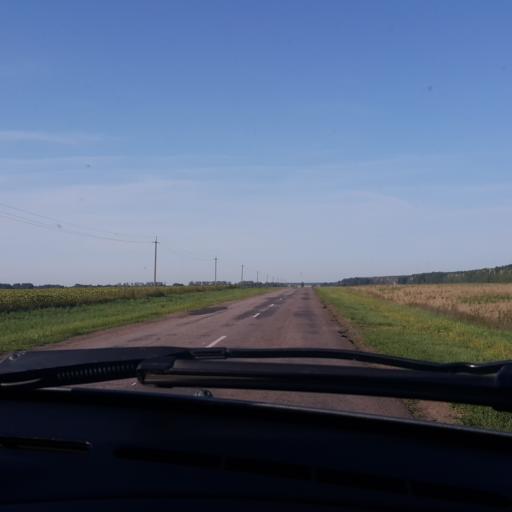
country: RU
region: Tambov
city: Novaya Lyada
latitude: 52.7678
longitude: 41.7412
